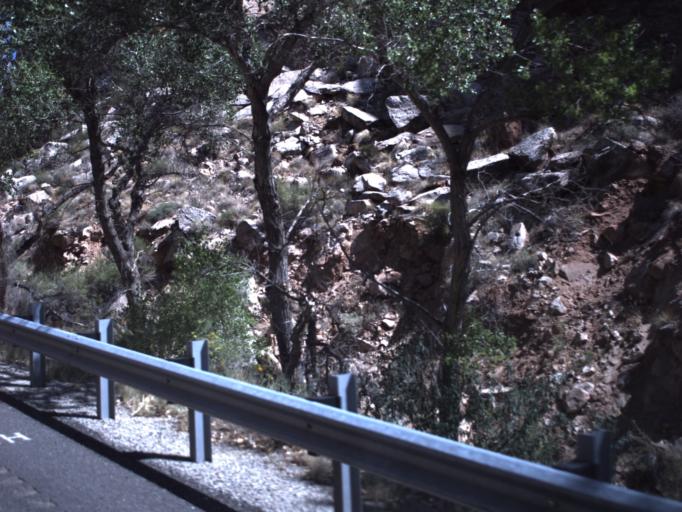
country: US
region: Utah
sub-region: San Juan County
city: Blanding
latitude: 37.2940
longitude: -109.5386
